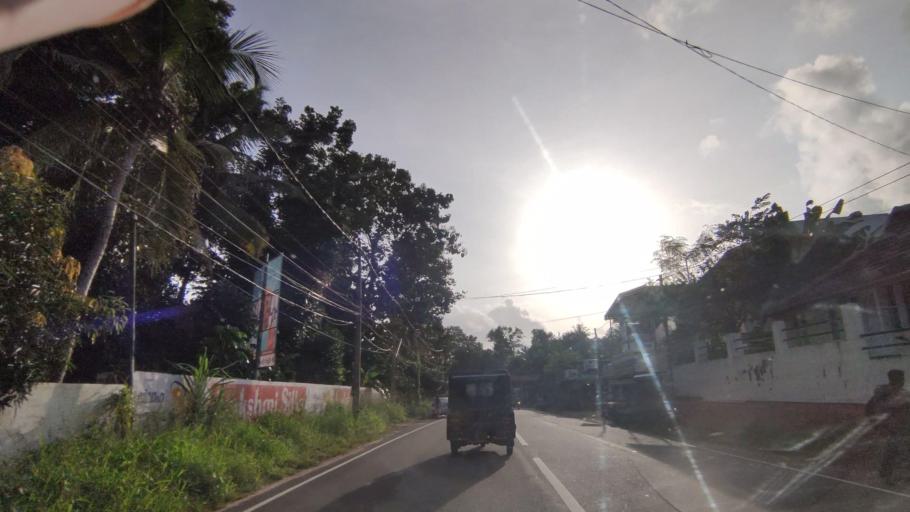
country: IN
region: Kerala
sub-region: Kottayam
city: Kottayam
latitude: 9.5958
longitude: 76.5089
